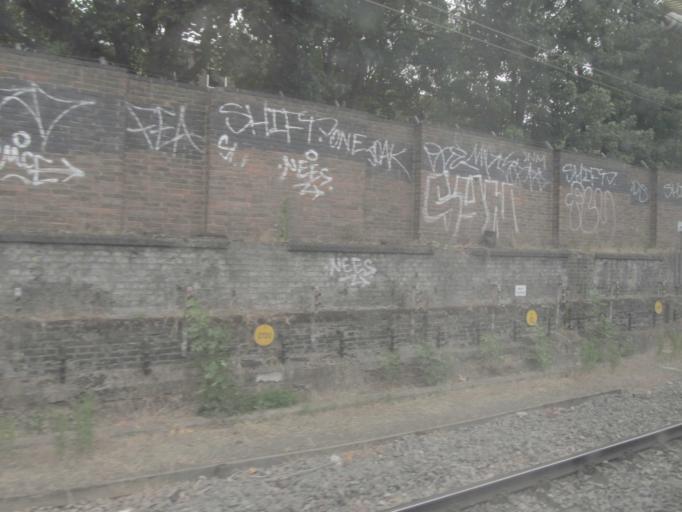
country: GB
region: England
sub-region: Greater London
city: Bayswater
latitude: 51.5242
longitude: -0.2123
